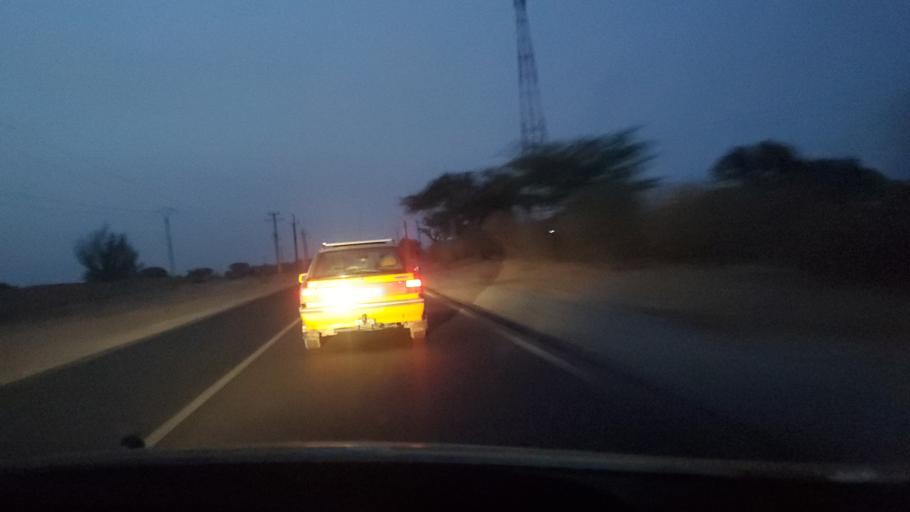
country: SN
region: Louga
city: Louga
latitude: 15.7175
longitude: -16.2728
